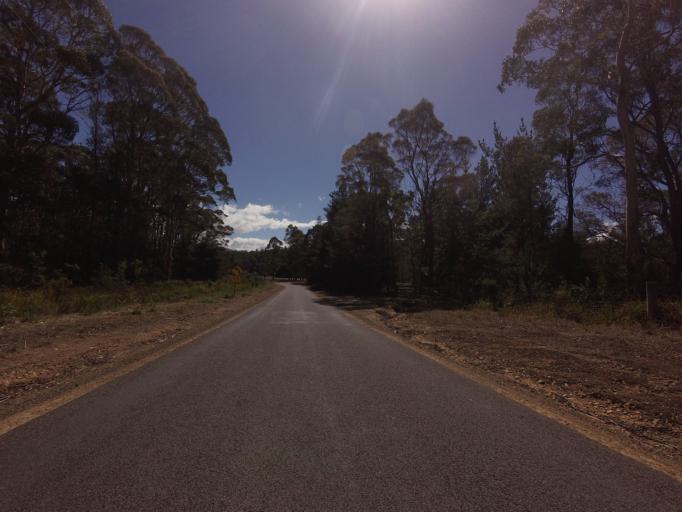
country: AU
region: Tasmania
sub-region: Break O'Day
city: St Helens
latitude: -41.5928
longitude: 148.2026
